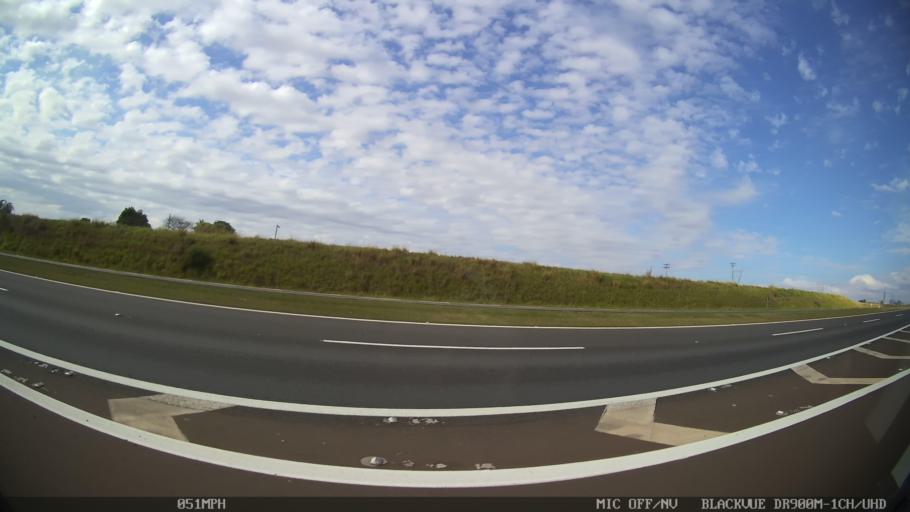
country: BR
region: Sao Paulo
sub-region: Iracemapolis
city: Iracemapolis
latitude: -22.6368
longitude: -47.4540
